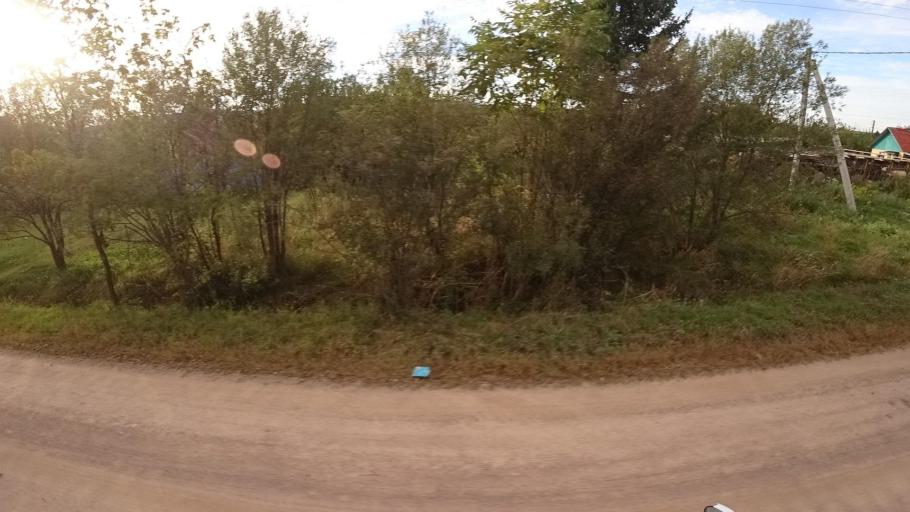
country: RU
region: Primorskiy
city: Yakovlevka
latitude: 44.4170
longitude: 133.4512
